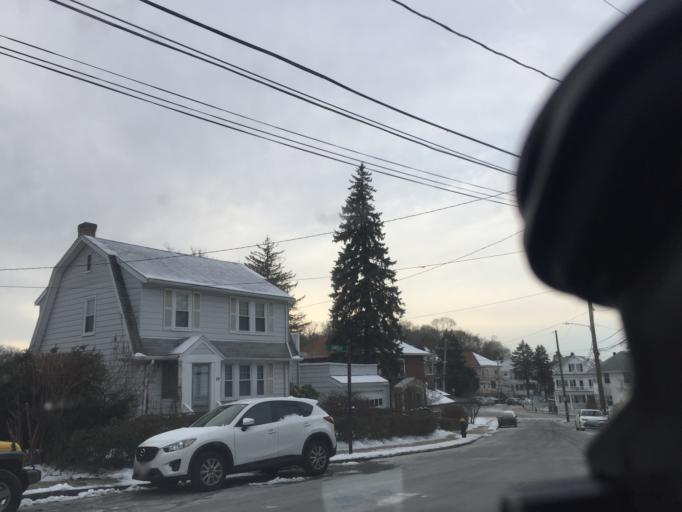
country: US
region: Massachusetts
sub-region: Middlesex County
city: Watertown
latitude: 42.3481
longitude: -71.1684
